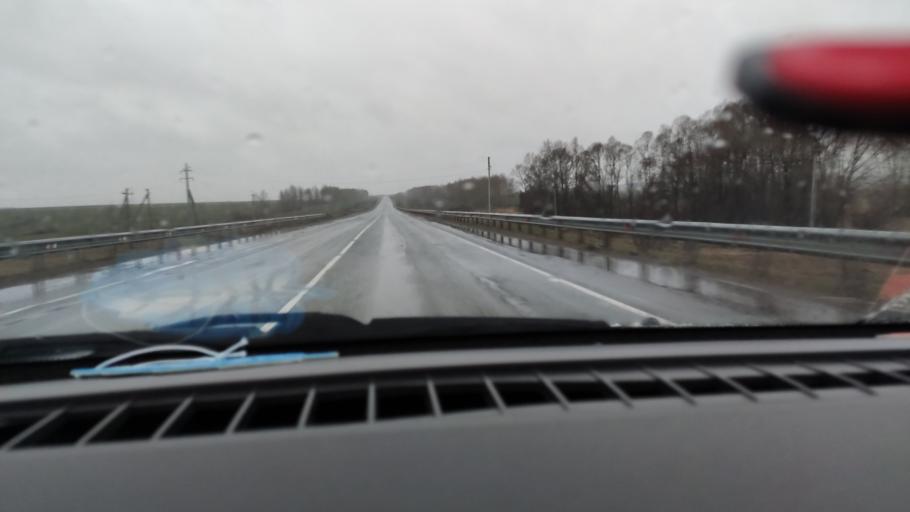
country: RU
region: Tatarstan
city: Mendeleyevsk
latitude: 55.9355
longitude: 52.2862
